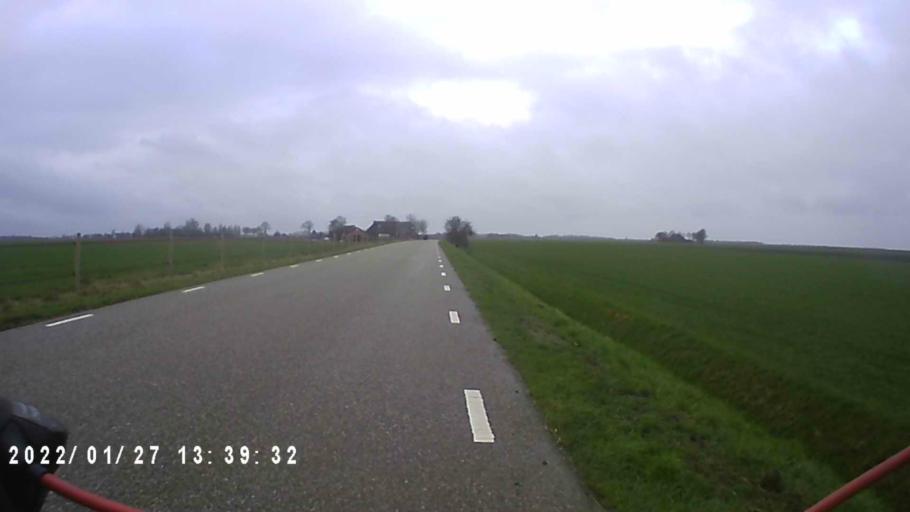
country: NL
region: Friesland
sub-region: Gemeente Kollumerland en Nieuwkruisland
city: Kollum
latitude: 53.2986
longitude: 6.2200
